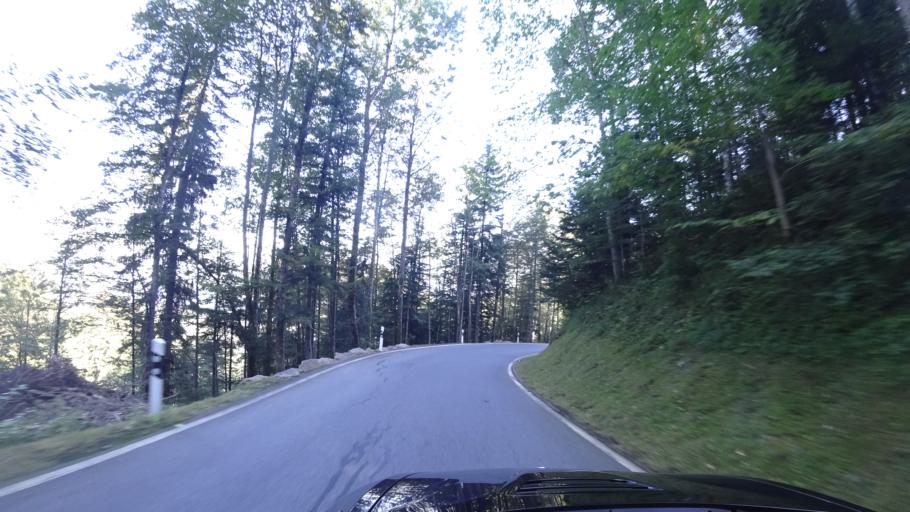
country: CH
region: Obwalden
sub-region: Obwalden
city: Giswil
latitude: 46.8289
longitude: 8.1312
